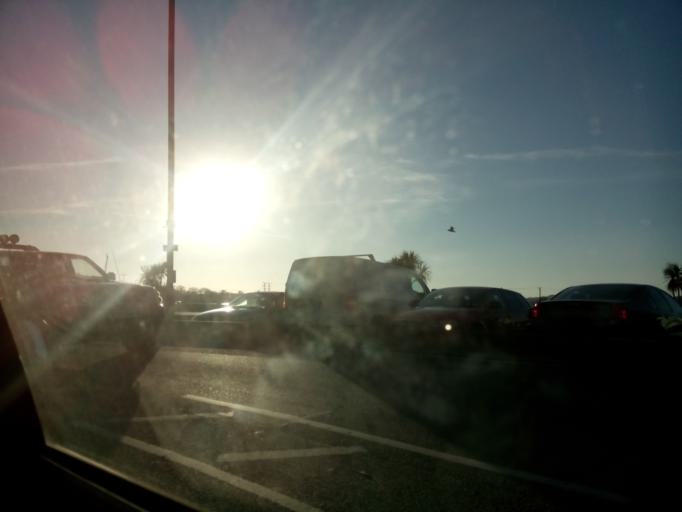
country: GB
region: England
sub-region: Cornwall
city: Hayle
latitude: 50.1878
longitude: -5.4230
